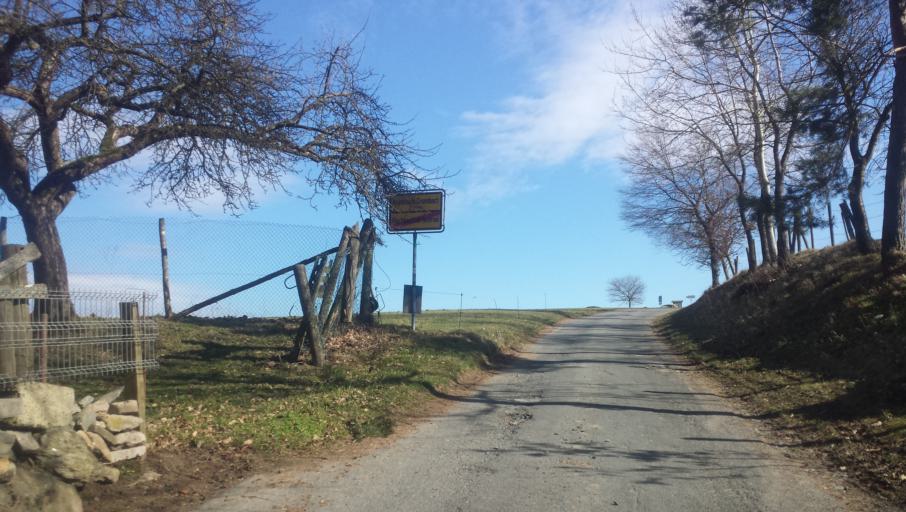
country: DE
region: Hesse
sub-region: Regierungsbezirk Darmstadt
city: Frankisch-Crumbach
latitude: 49.7521
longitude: 8.8245
